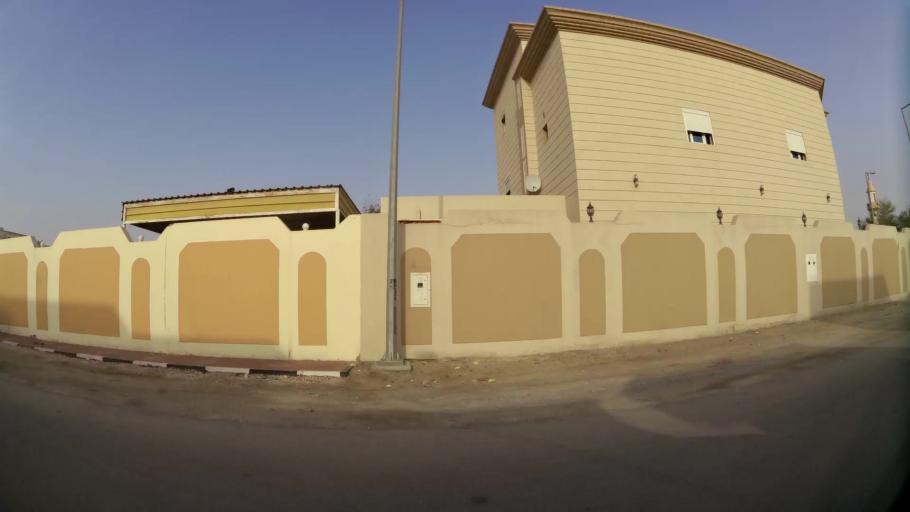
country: QA
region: Baladiyat ar Rayyan
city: Ar Rayyan
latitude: 25.2495
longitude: 51.4463
